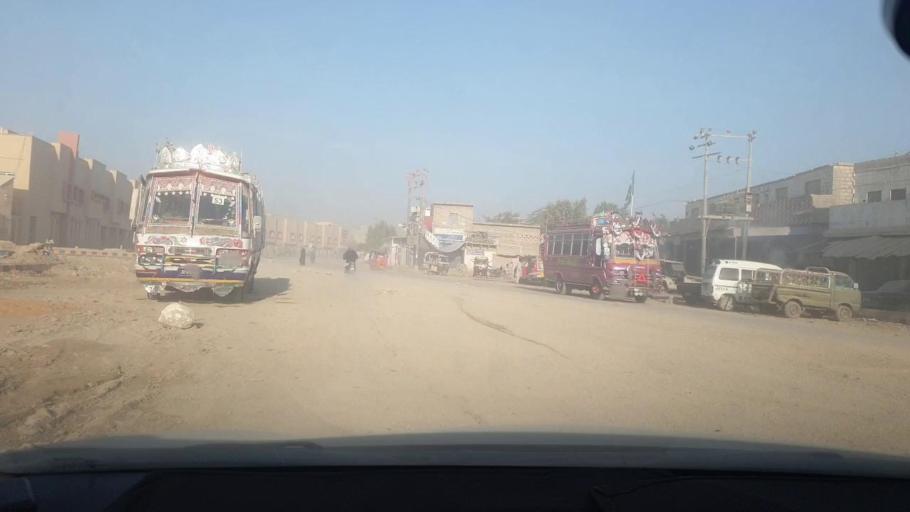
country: PK
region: Sindh
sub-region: Karachi District
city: Karachi
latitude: 24.9767
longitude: 67.0380
